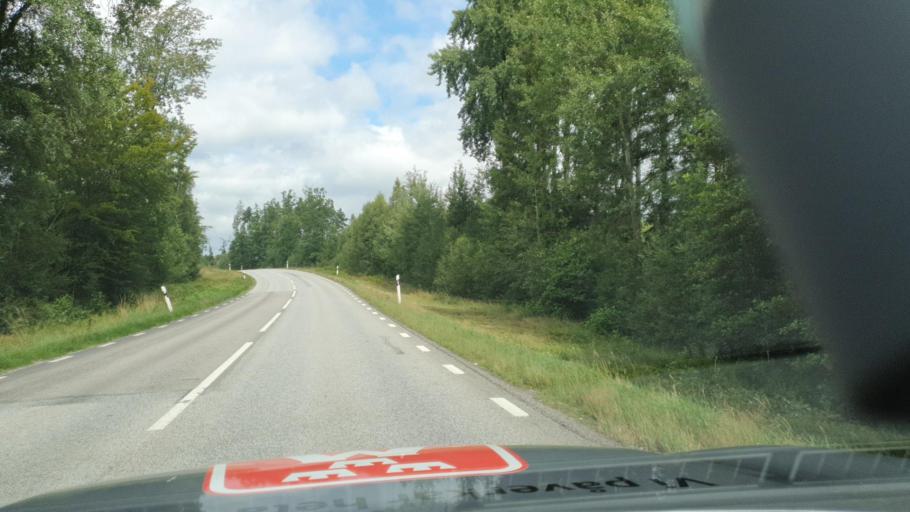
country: SE
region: Blekinge
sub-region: Karlskrona Kommun
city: Rodeby
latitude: 56.2950
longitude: 15.5837
